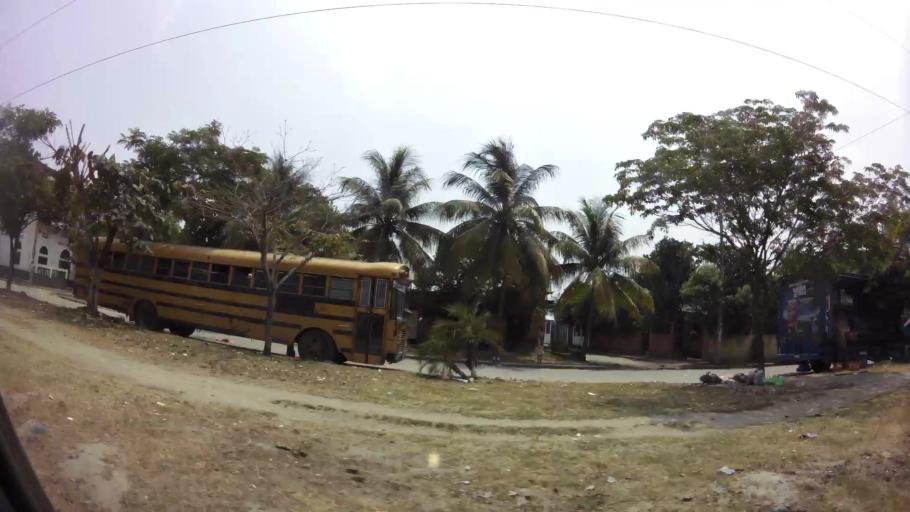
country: HN
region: Cortes
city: San Pedro Sula
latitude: 15.4876
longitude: -87.9852
